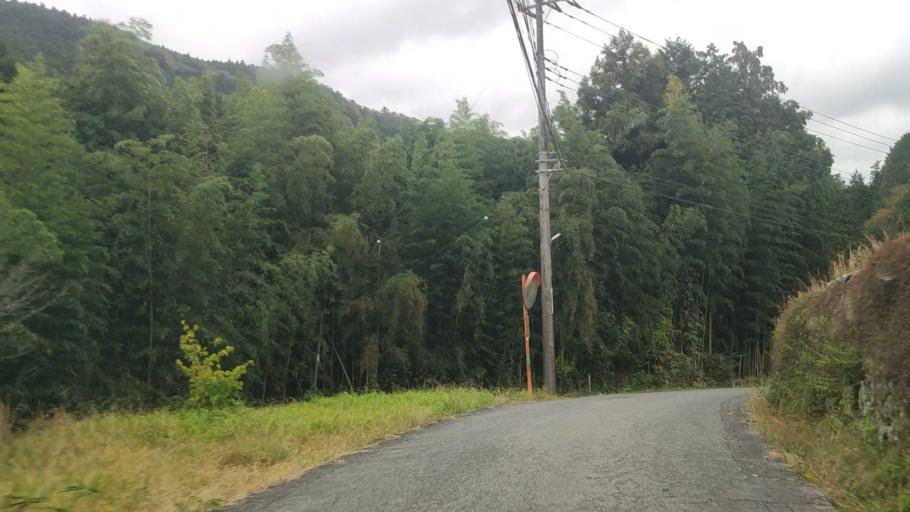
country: JP
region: Shizuoka
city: Ito
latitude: 34.9057
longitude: 138.9691
